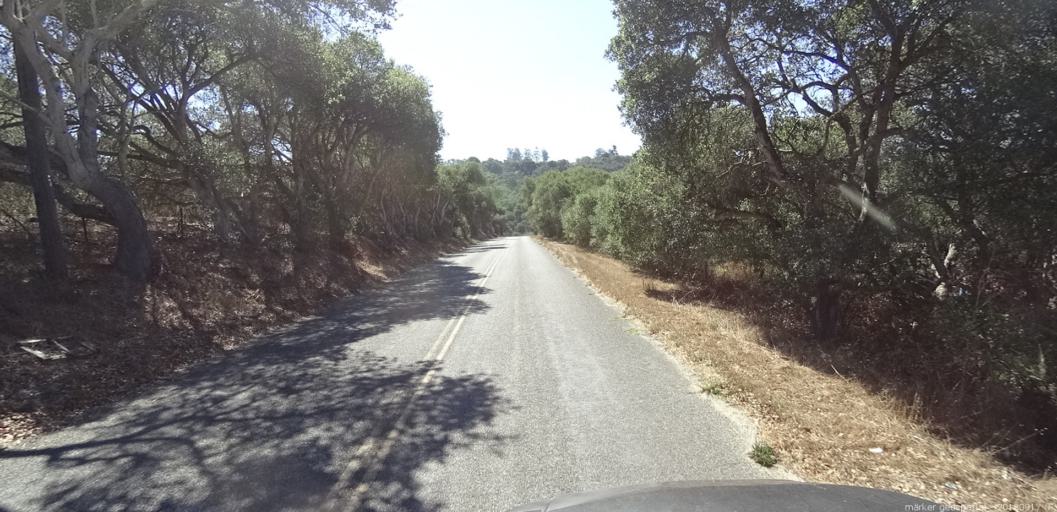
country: US
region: California
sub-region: Monterey County
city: Elkhorn
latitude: 36.8348
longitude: -121.6959
